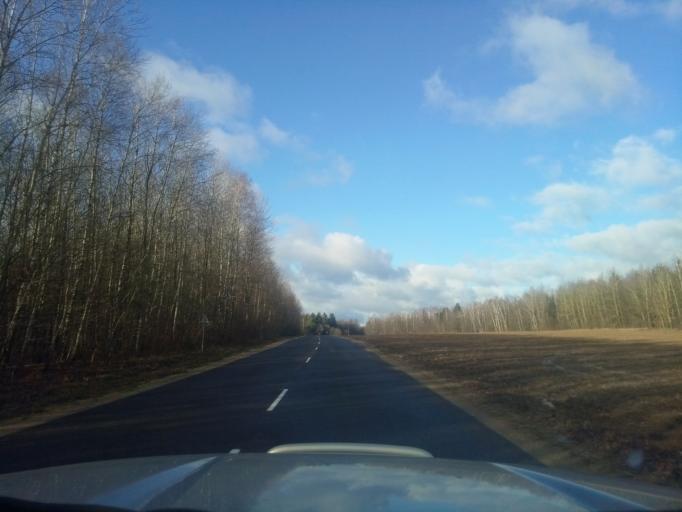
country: BY
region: Minsk
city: Kapyl'
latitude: 53.1724
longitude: 27.0237
